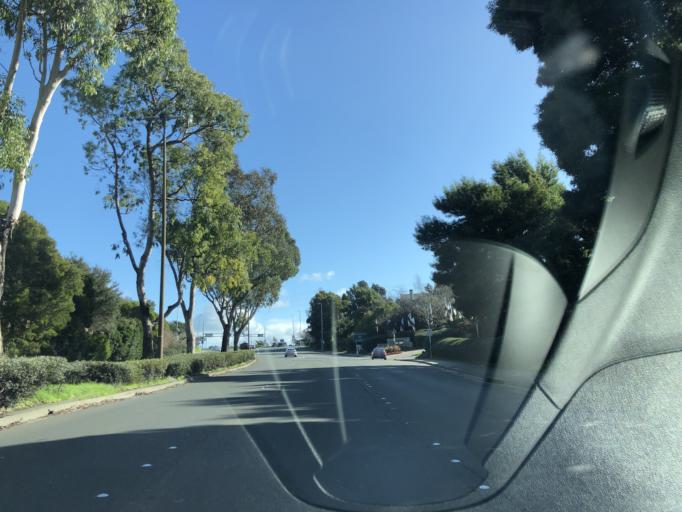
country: US
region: California
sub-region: Contra Costa County
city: Tara Hills
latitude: 37.9880
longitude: -122.3200
